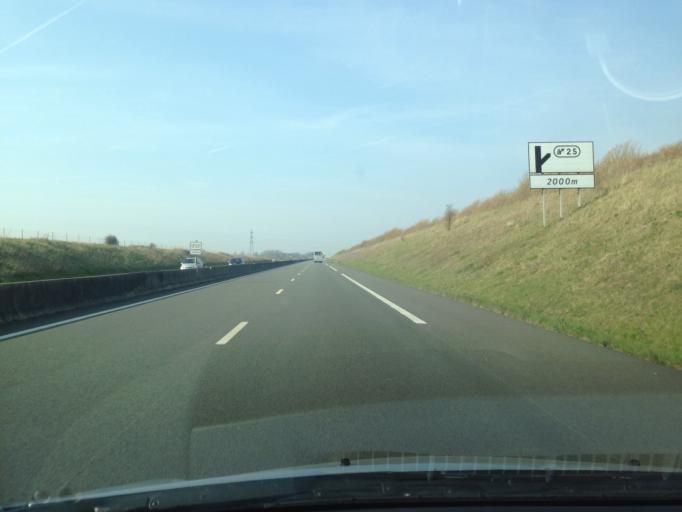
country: FR
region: Nord-Pas-de-Calais
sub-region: Departement du Pas-de-Calais
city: Verton
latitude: 50.3867
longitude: 1.6960
